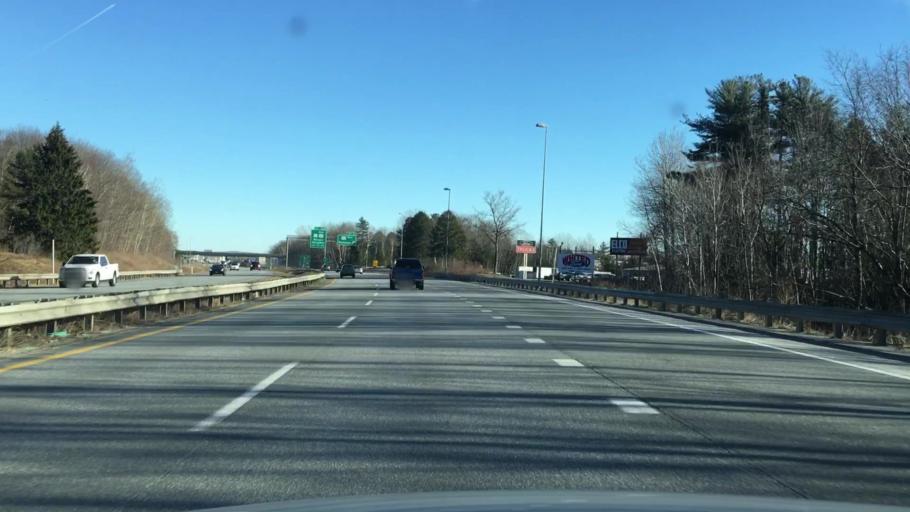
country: US
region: Maine
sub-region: Penobscot County
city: Bangor
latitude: 44.7861
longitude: -68.8008
